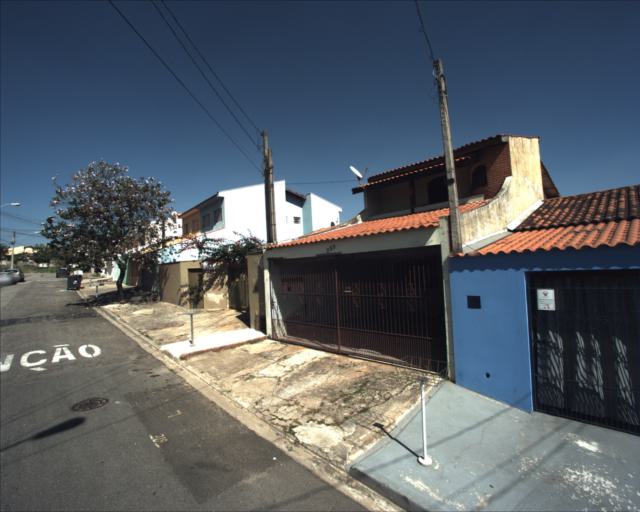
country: BR
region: Sao Paulo
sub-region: Sorocaba
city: Sorocaba
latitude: -23.4926
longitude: -47.4218
